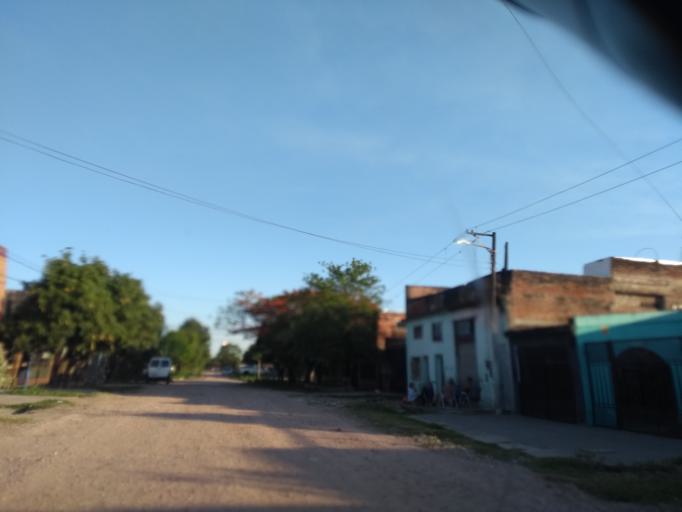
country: AR
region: Chaco
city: Barranqueras
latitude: -27.4850
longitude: -58.9430
